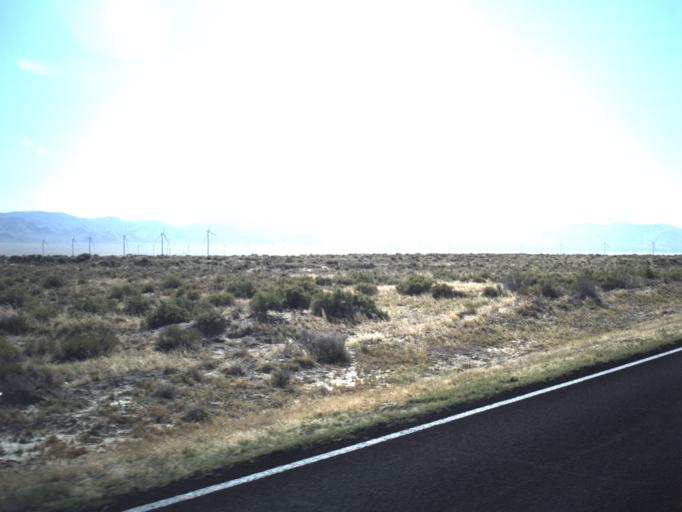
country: US
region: Utah
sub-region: Beaver County
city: Milford
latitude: 38.5471
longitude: -112.9912
